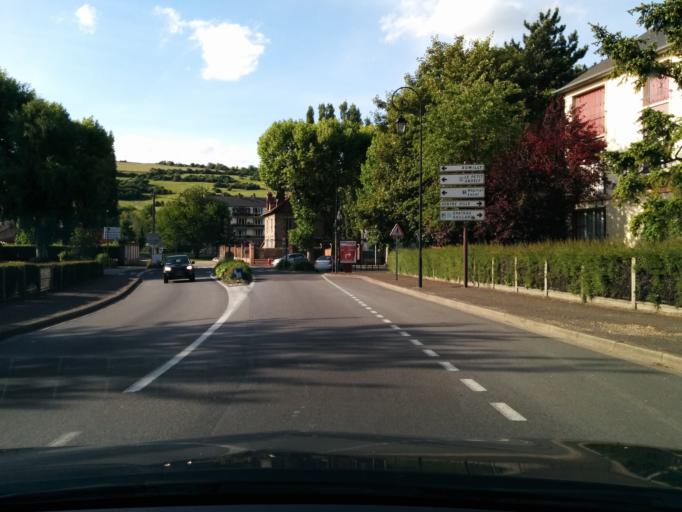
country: FR
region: Haute-Normandie
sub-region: Departement de l'Eure
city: Les Andelys
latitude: 49.2429
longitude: 1.4035
